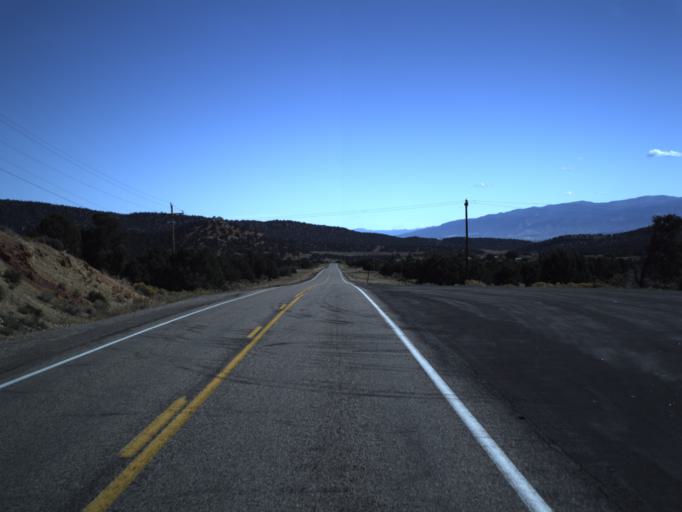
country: US
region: Utah
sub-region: Iron County
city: Cedar City
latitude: 37.6253
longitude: -113.3175
